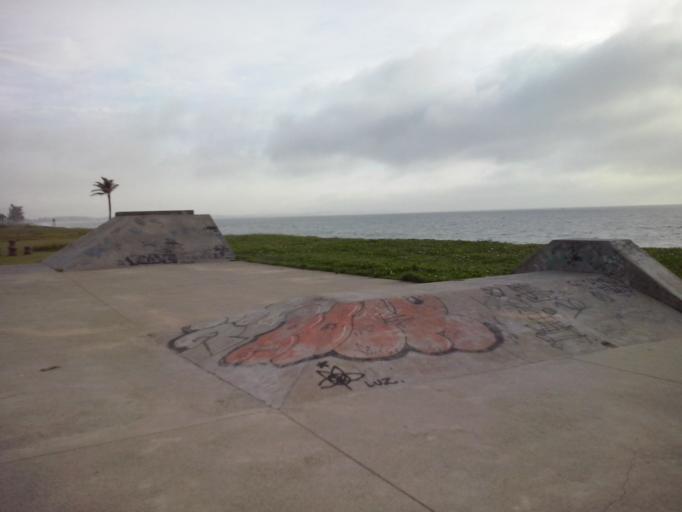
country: BR
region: Rio de Janeiro
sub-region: Rio Das Ostras
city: Rio das Ostras
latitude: -22.5860
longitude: -41.9873
